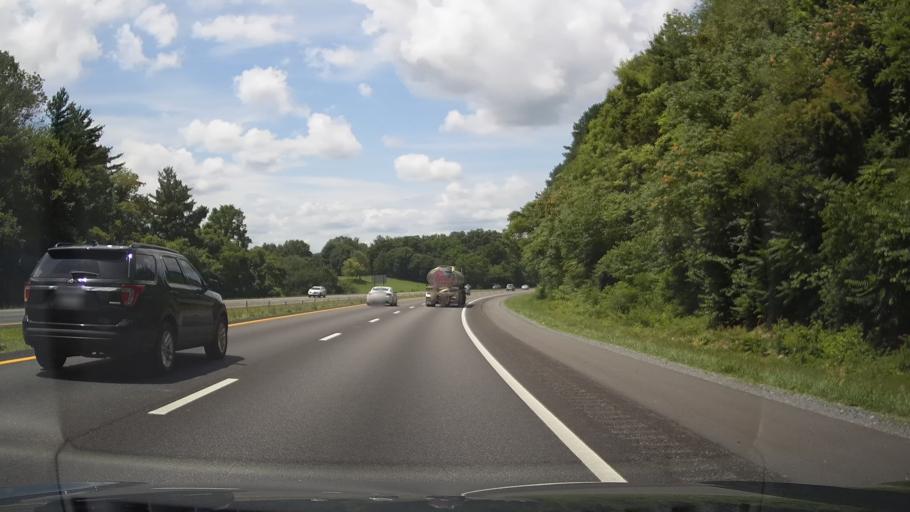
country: US
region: Tennessee
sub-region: Washington County
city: Oak Grove
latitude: 36.3634
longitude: -82.4093
